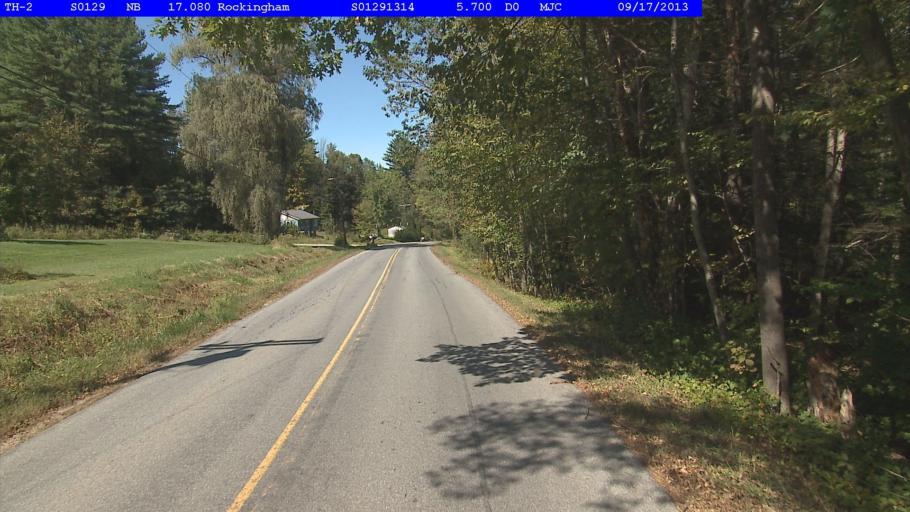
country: US
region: Vermont
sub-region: Windham County
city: Rockingham
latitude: 43.1985
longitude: -72.5120
